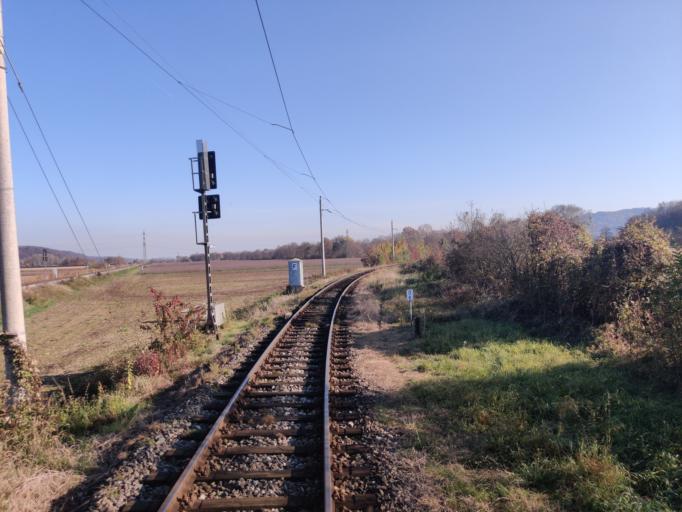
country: AT
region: Styria
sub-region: Politischer Bezirk Suedoststeiermark
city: Feldbach
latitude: 46.9583
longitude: 15.8962
